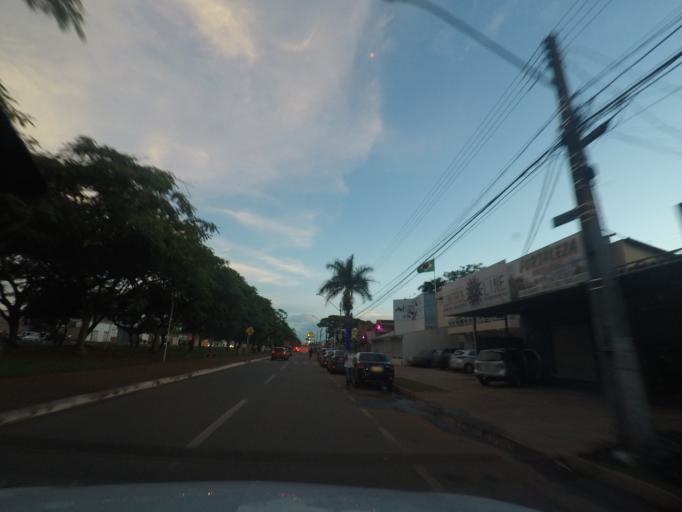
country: BR
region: Goias
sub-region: Goiania
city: Goiania
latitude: -16.7062
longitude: -49.3113
